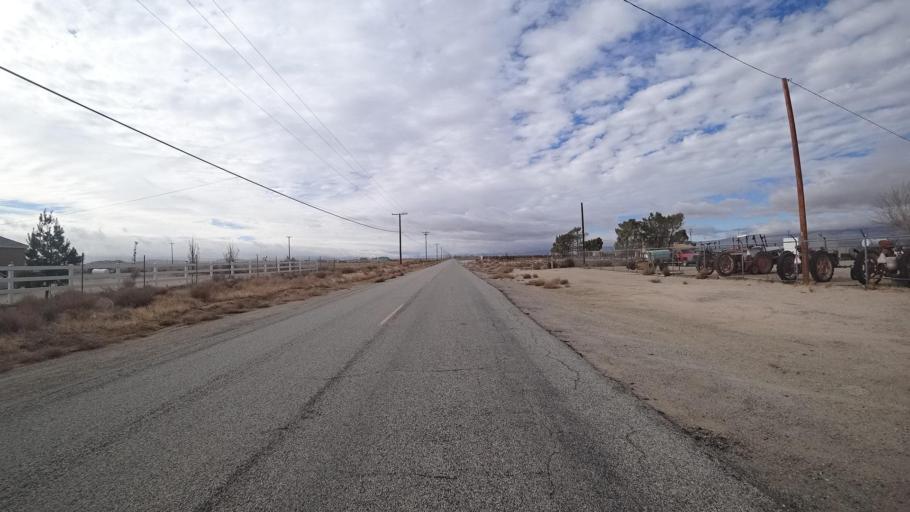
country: US
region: California
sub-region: Kern County
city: Rosamond
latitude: 34.8201
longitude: -118.2801
